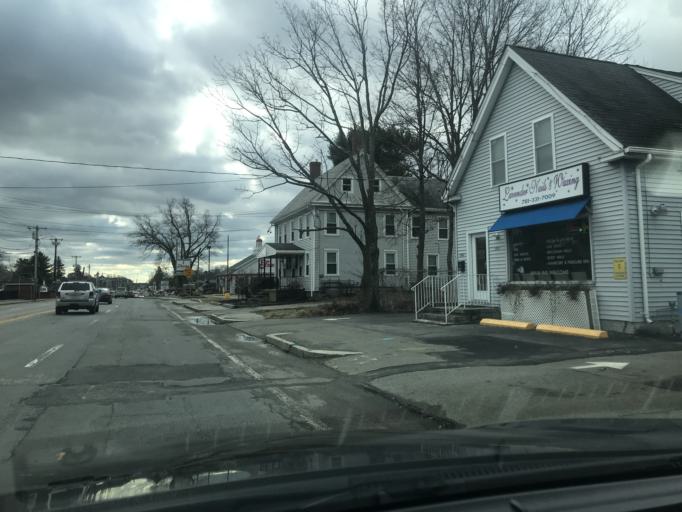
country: US
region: Massachusetts
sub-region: Norfolk County
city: Weymouth
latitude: 42.1707
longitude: -70.9554
